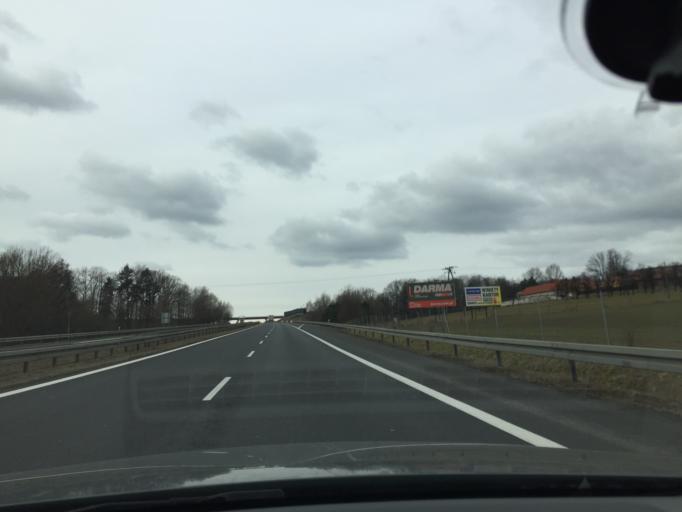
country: PL
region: Silesian Voivodeship
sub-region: Powiat cieszynski
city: Zamarski
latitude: 49.7636
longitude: 18.6690
